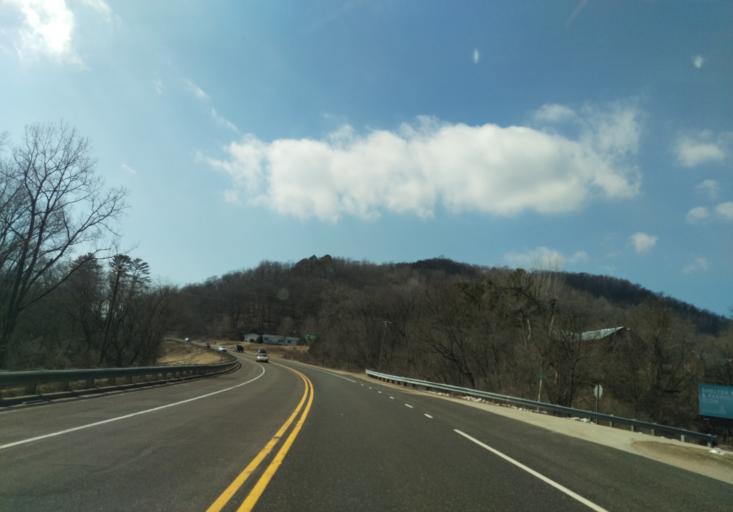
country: US
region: Wisconsin
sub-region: La Crosse County
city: La Crosse
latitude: 43.7691
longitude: -91.1605
